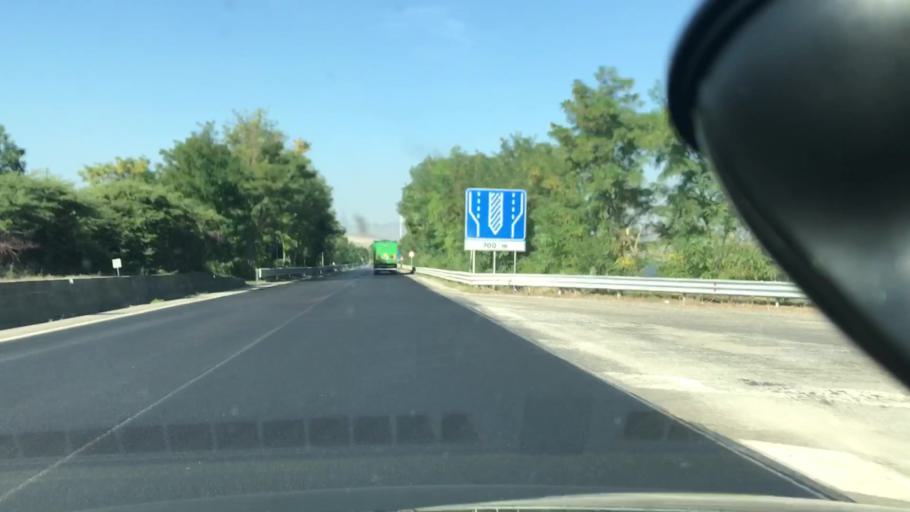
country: IT
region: Basilicate
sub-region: Provincia di Potenza
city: Zona 179
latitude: 41.0824
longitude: 15.6177
